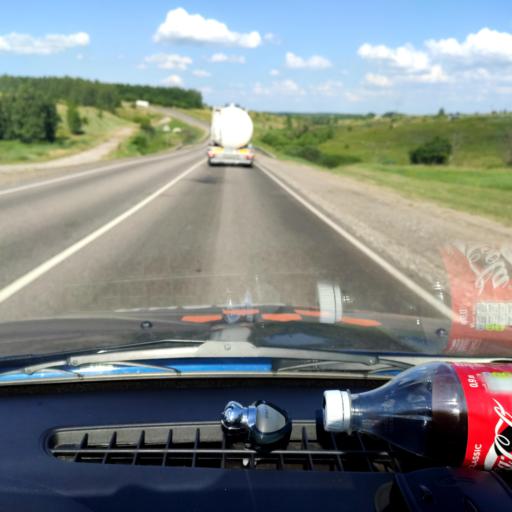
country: RU
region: Lipetsk
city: Kazaki
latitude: 52.5879
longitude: 38.2303
